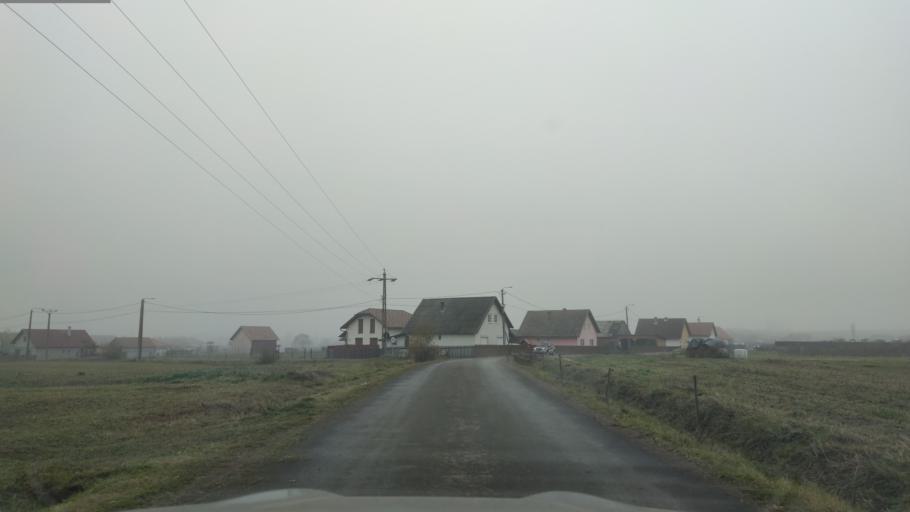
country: RO
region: Harghita
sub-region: Comuna Remetea
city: Remetea
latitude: 46.8062
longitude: 25.4396
